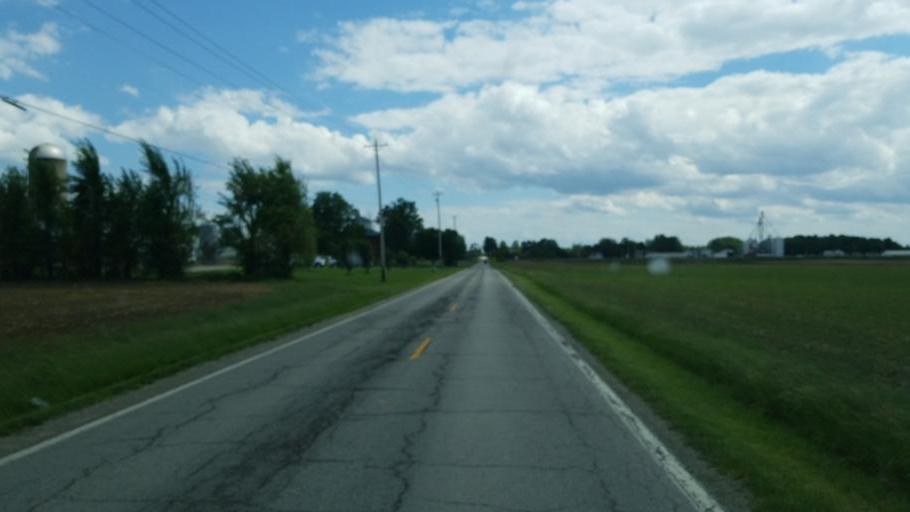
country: US
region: Ohio
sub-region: Huron County
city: Plymouth
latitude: 41.0590
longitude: -82.6100
